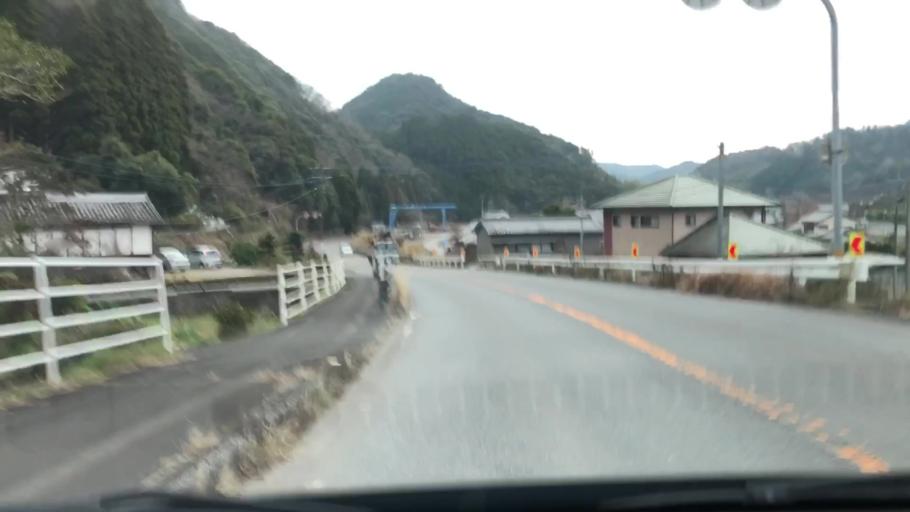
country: JP
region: Oita
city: Saiki
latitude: 32.9892
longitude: 131.8336
